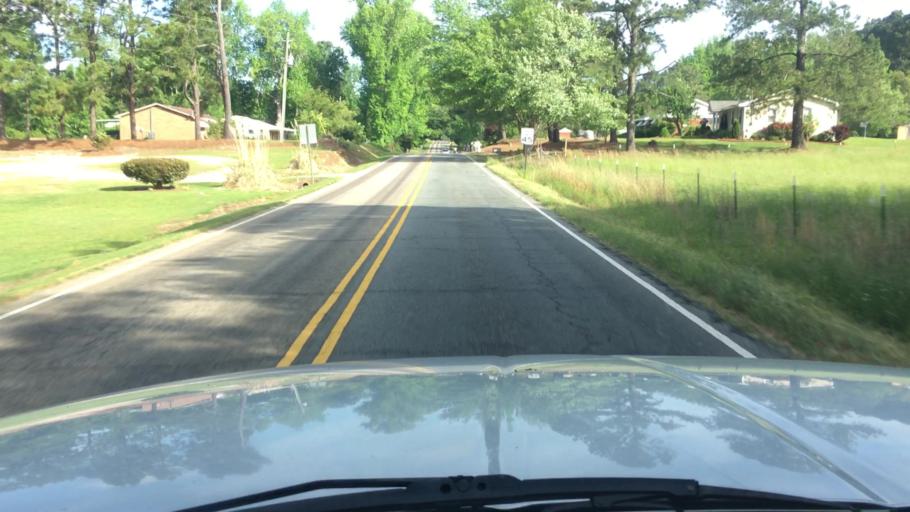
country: US
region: North Carolina
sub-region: Johnston County
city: Wilsons Mills
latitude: 35.6362
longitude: -78.3342
